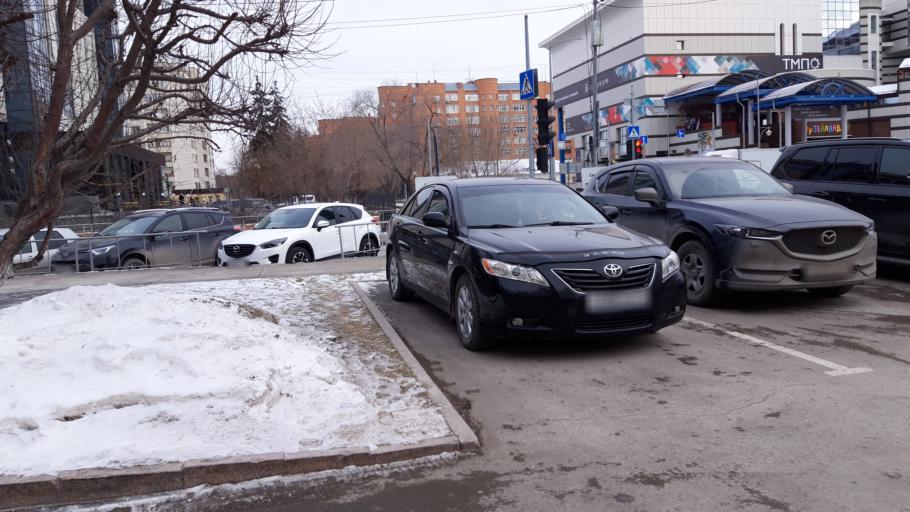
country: RU
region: Tjumen
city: Tyumen
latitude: 57.1537
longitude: 65.5480
